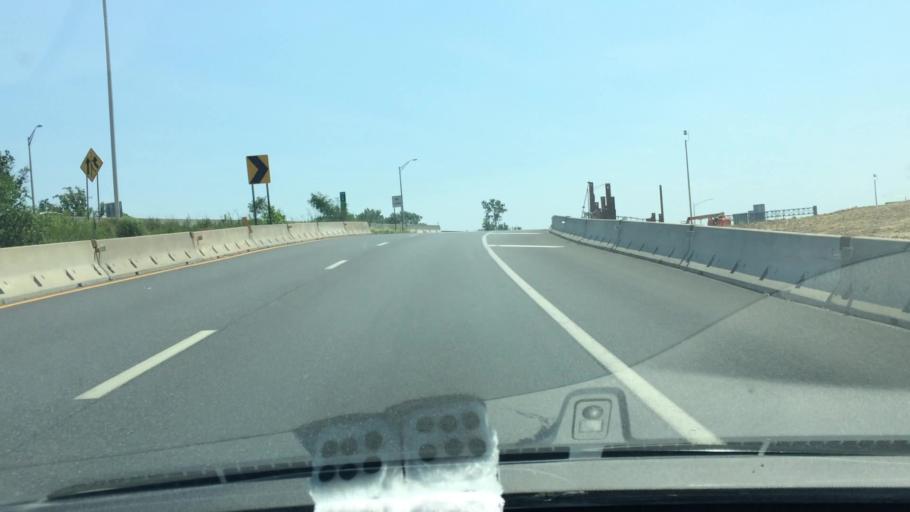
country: US
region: New Jersey
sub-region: Camden County
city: Bellmawr
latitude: 39.8671
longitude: -75.1031
